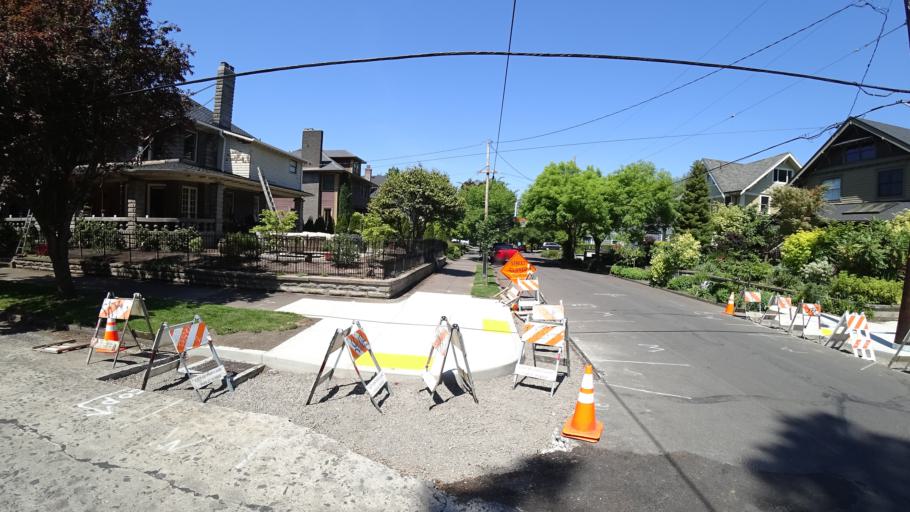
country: US
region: Oregon
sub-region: Multnomah County
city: Portland
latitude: 45.5404
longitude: -122.6392
